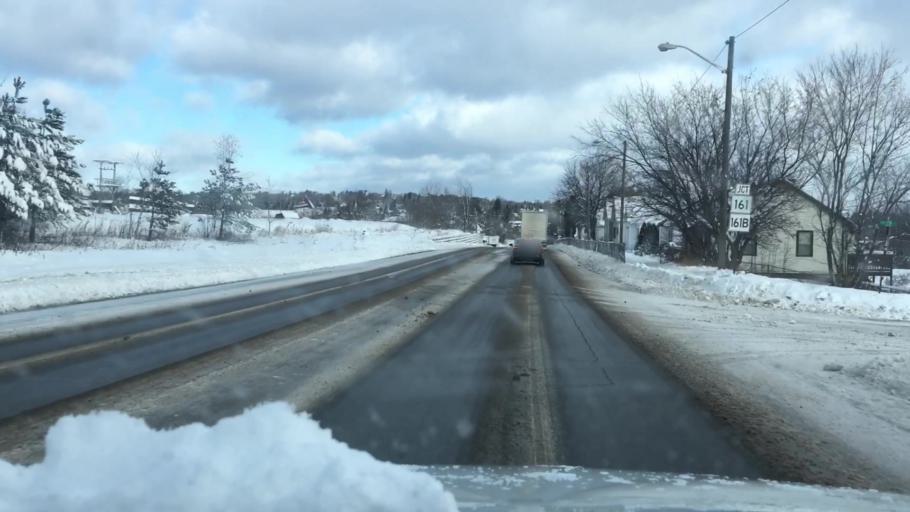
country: US
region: Maine
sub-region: Aroostook County
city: Caribou
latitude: 46.8515
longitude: -68.0053
